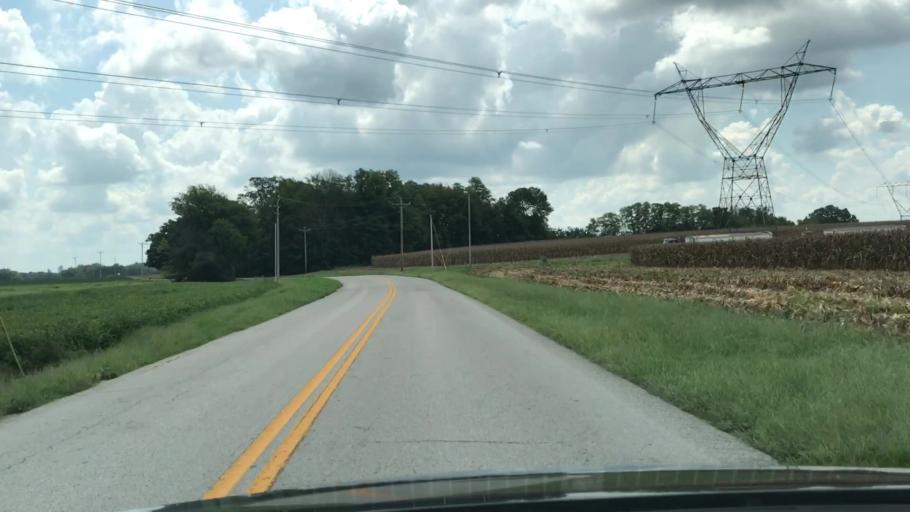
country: US
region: Kentucky
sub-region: Todd County
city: Elkton
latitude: 36.7727
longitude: -87.1175
